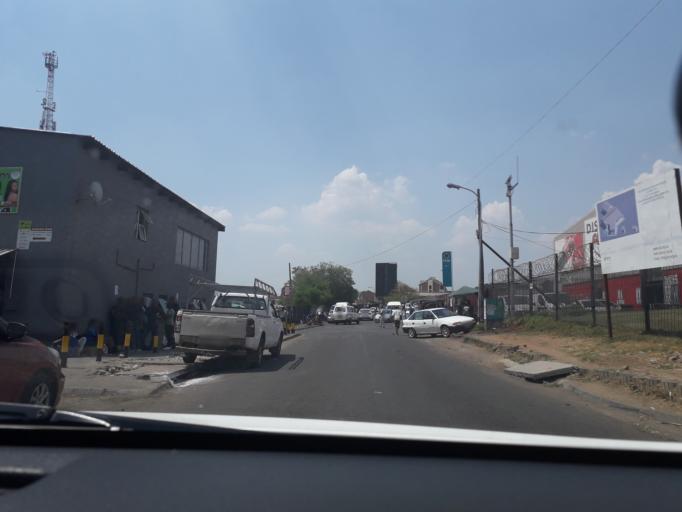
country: ZA
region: Gauteng
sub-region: City of Johannesburg Metropolitan Municipality
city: Midrand
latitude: -25.9987
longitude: 28.1286
